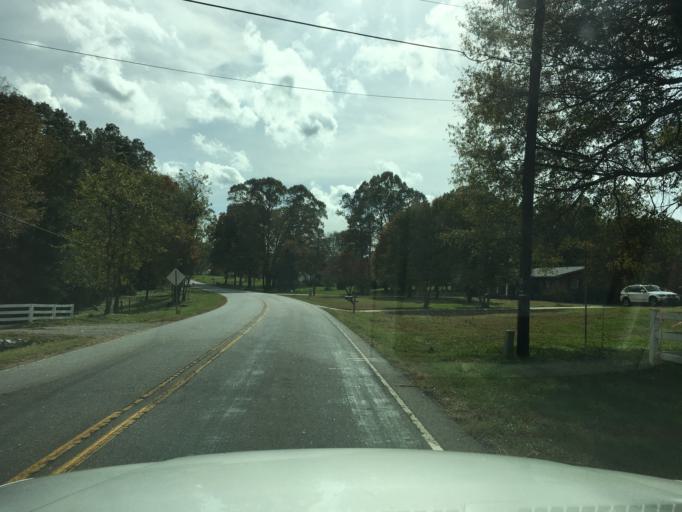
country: US
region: North Carolina
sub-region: Catawba County
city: Newton
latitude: 35.6765
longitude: -81.2736
